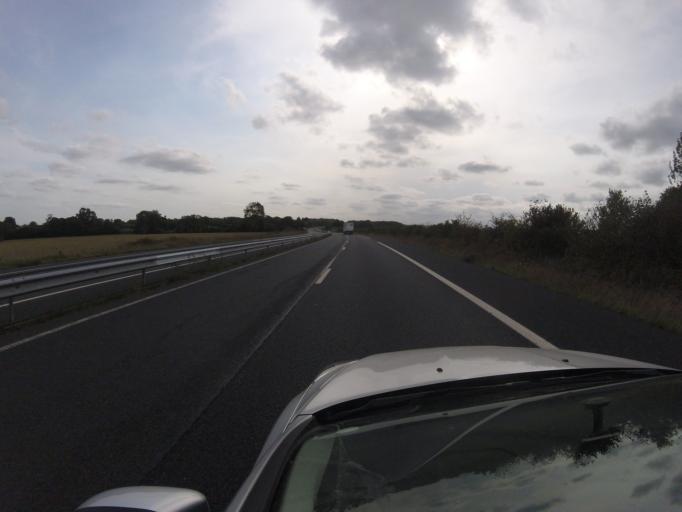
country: FR
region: Lower Normandy
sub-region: Departement de la Manche
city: Pont-Hebert
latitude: 49.1796
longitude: -1.1466
